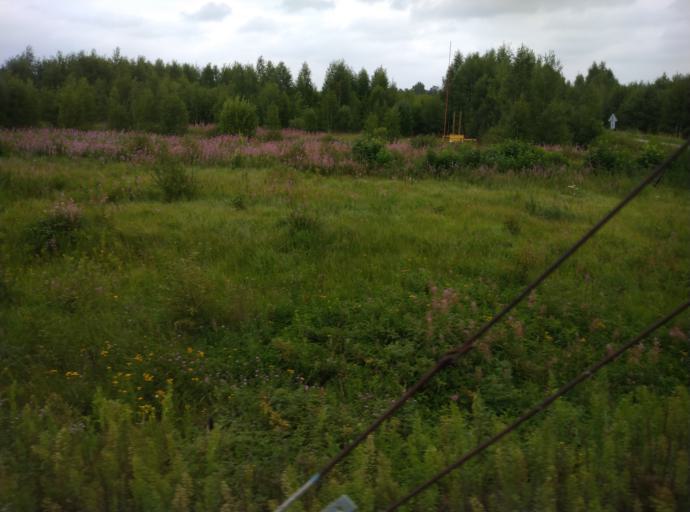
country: RU
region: Kostroma
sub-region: Kostromskoy Rayon
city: Kostroma
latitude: 57.7119
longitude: 40.8622
